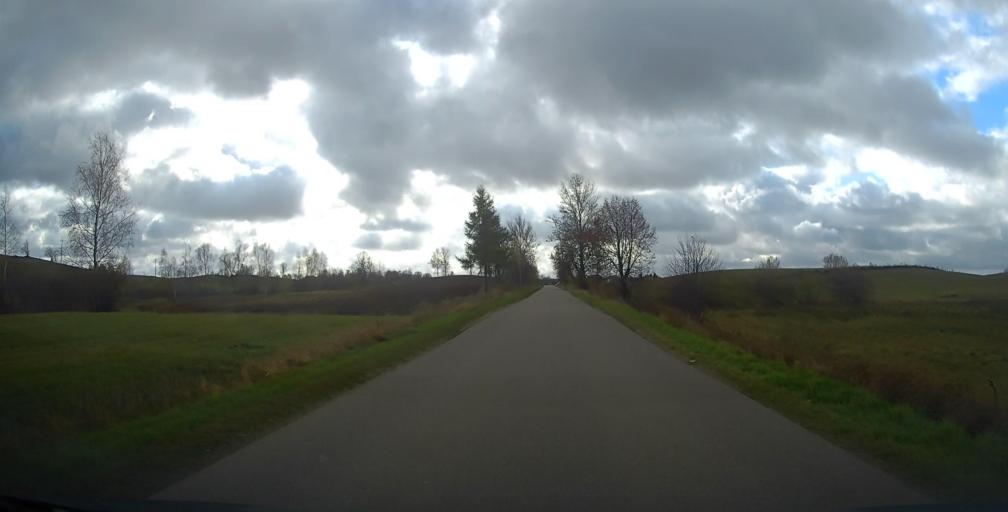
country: PL
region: Podlasie
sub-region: Suwalki
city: Suwalki
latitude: 54.3489
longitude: 22.8560
